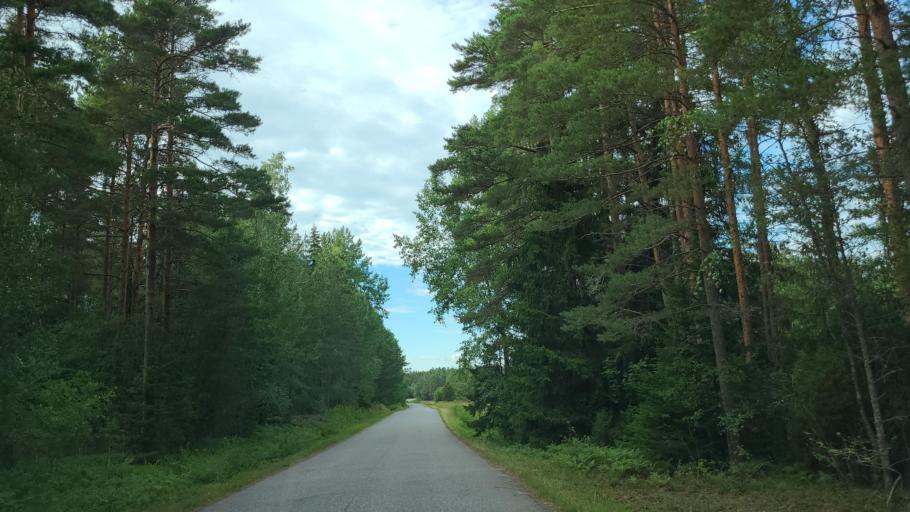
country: FI
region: Varsinais-Suomi
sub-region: Turku
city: Rymaettylae
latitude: 60.3028
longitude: 21.9420
